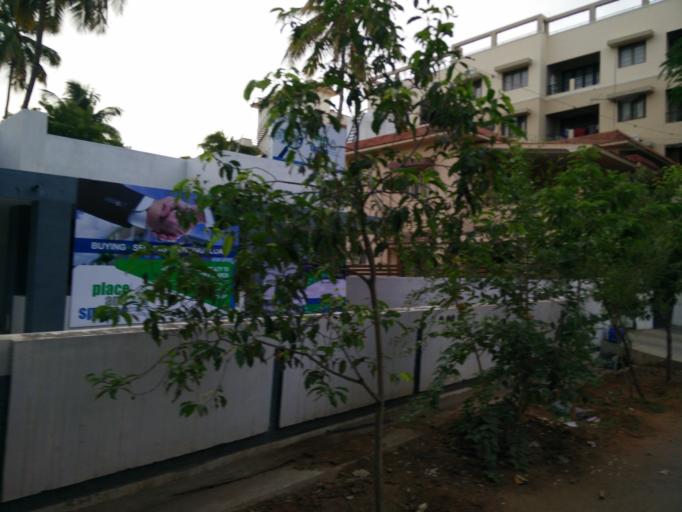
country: IN
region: Tamil Nadu
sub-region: Coimbatore
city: Coimbatore
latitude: 11.0234
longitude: 76.9441
